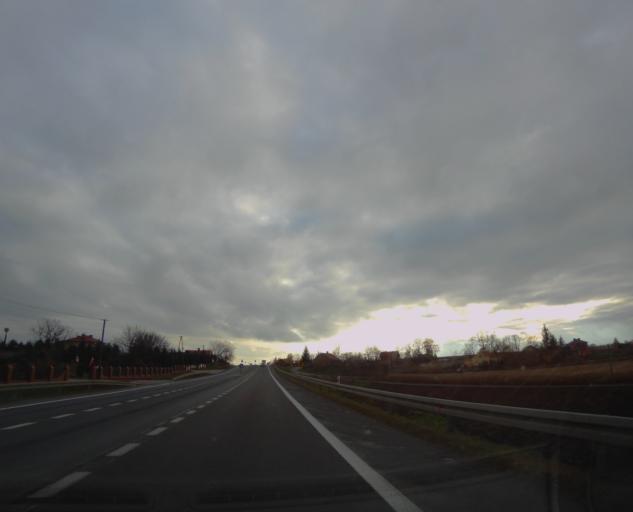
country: PL
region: Subcarpathian Voivodeship
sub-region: Powiat jaroslawski
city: Radymno
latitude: 49.9262
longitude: 22.8213
